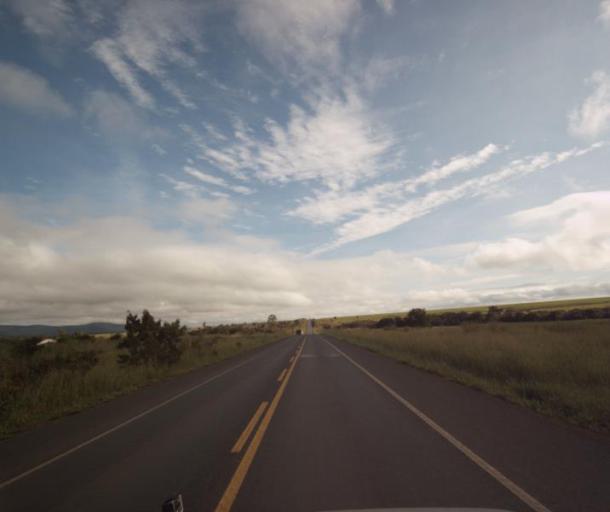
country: BR
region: Goias
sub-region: Padre Bernardo
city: Padre Bernardo
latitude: -15.4388
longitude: -48.6192
